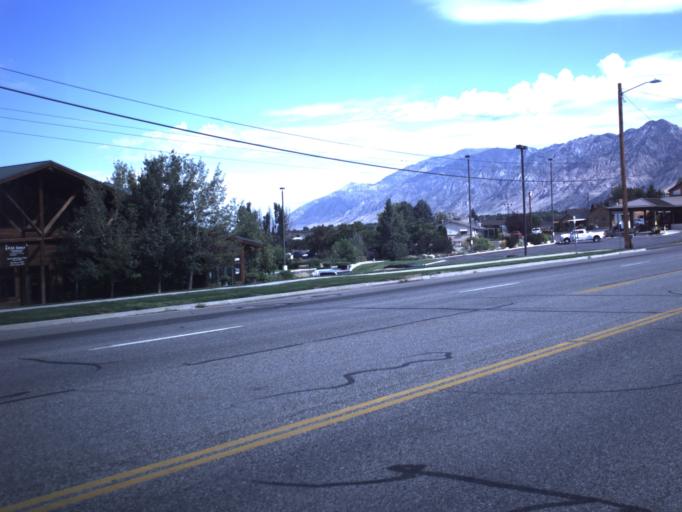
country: US
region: Utah
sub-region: Box Elder County
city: Perry
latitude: 41.4740
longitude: -112.0259
